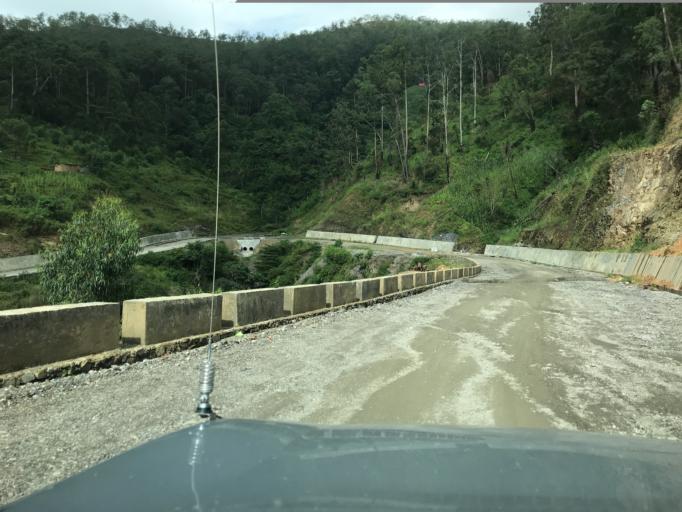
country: TL
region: Aileu
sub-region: Aileu Villa
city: Aileu
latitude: -8.6605
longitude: 125.5317
